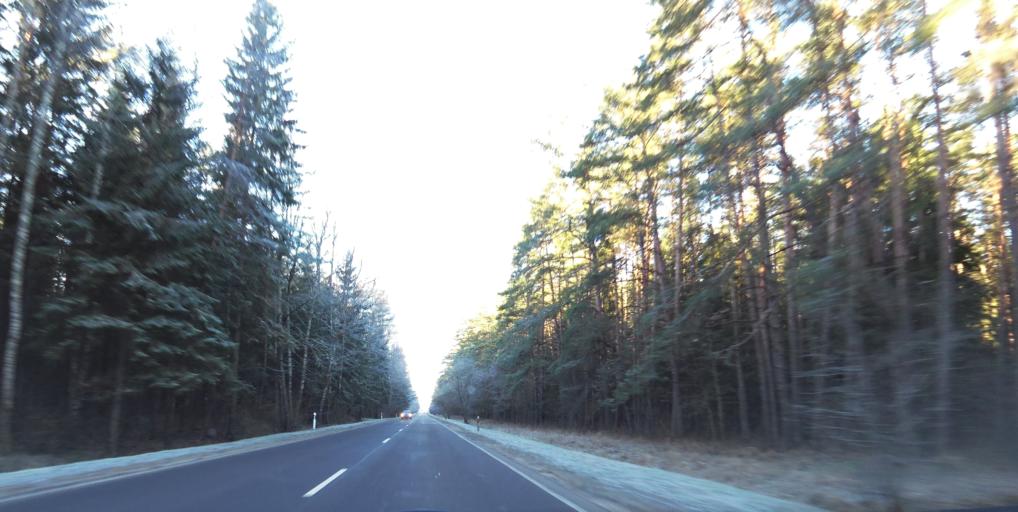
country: LT
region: Vilnius County
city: Lazdynai
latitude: 54.6430
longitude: 25.1659
